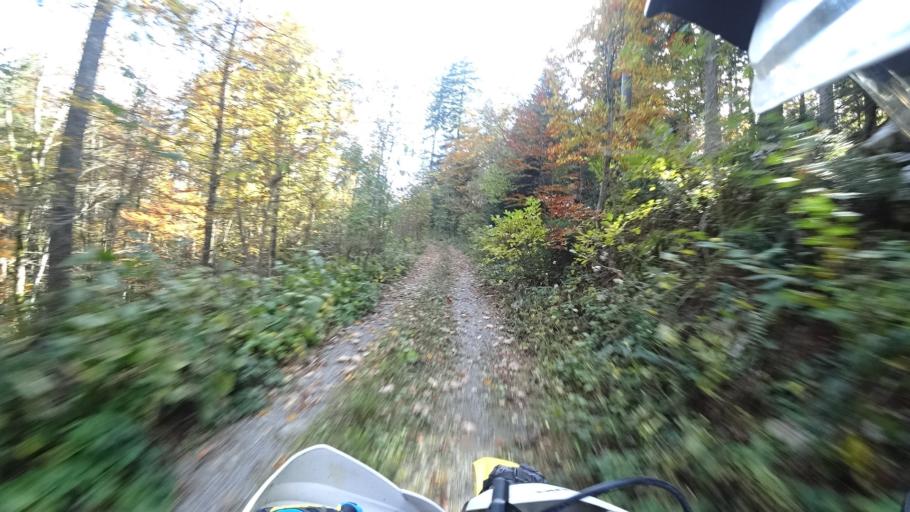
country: HR
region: Karlovacka
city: Plaski
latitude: 45.0630
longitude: 15.3228
